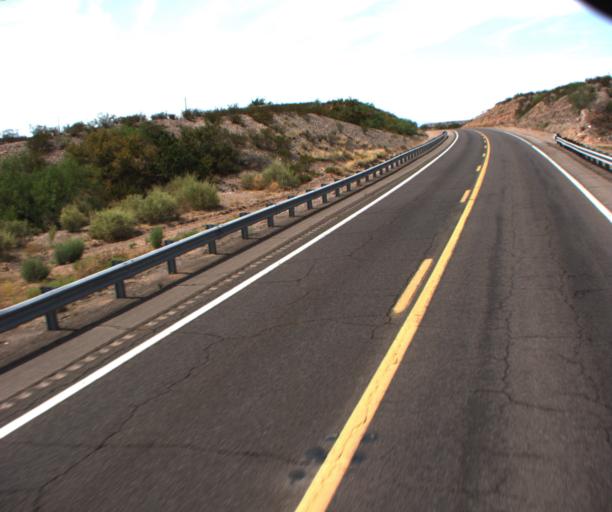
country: US
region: Arizona
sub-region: Greenlee County
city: Clifton
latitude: 32.8077
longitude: -109.1676
